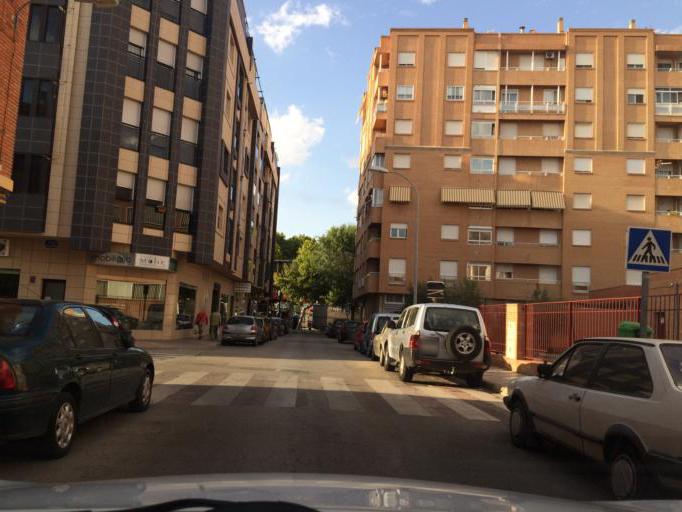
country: ES
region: Castille-La Mancha
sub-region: Provincia de Albacete
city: Albacete
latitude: 38.9956
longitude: -1.8659
